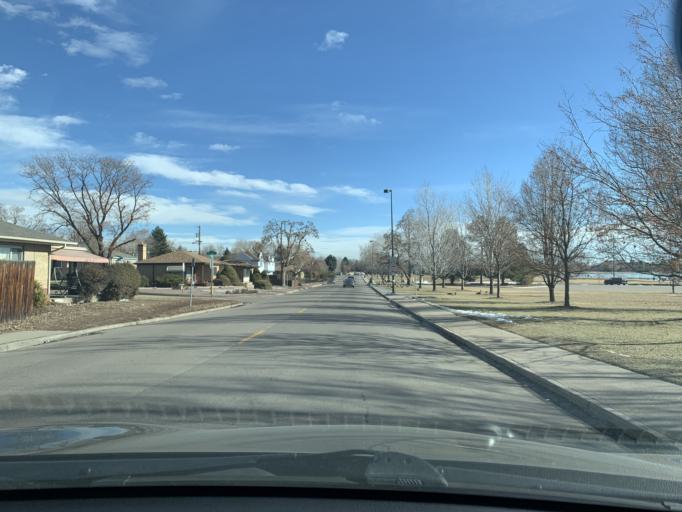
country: US
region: Colorado
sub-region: Jefferson County
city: Edgewater
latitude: 39.7530
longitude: -105.0527
